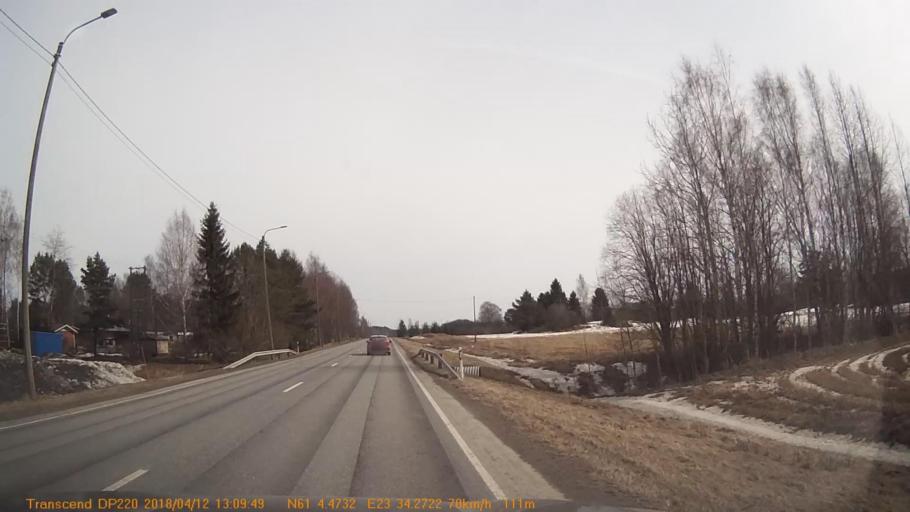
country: FI
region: Pirkanmaa
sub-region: Etelae-Pirkanmaa
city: Urjala
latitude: 61.0743
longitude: 23.5727
